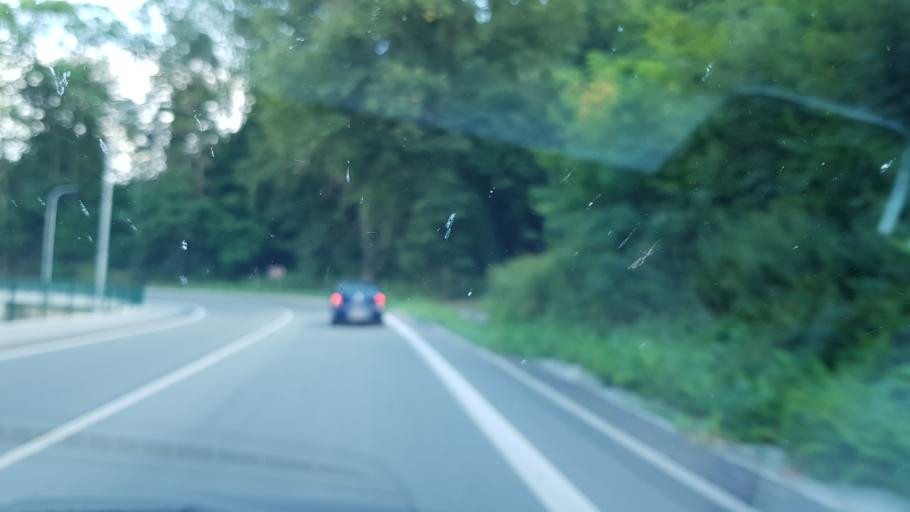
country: CZ
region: Pardubicky
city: Zamberk
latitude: 50.0876
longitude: 16.4583
